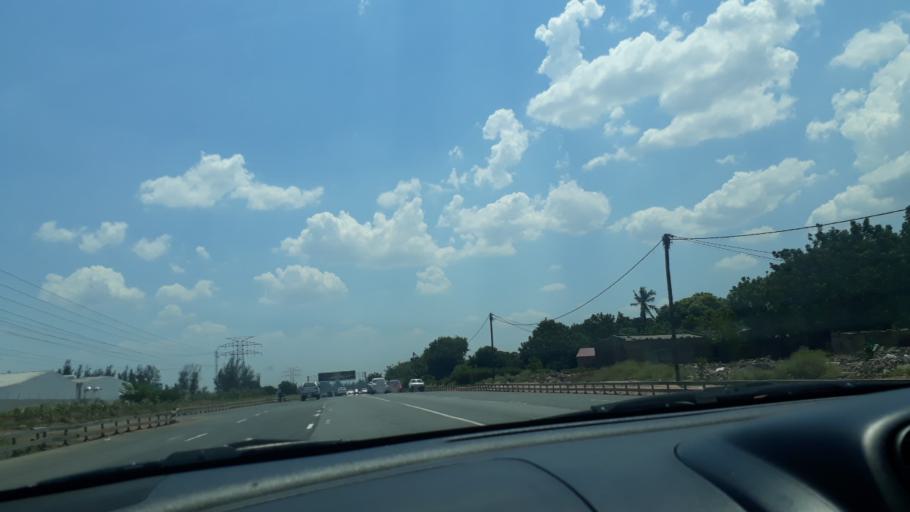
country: MZ
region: Maputo
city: Matola
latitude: -25.9343
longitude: 32.5006
